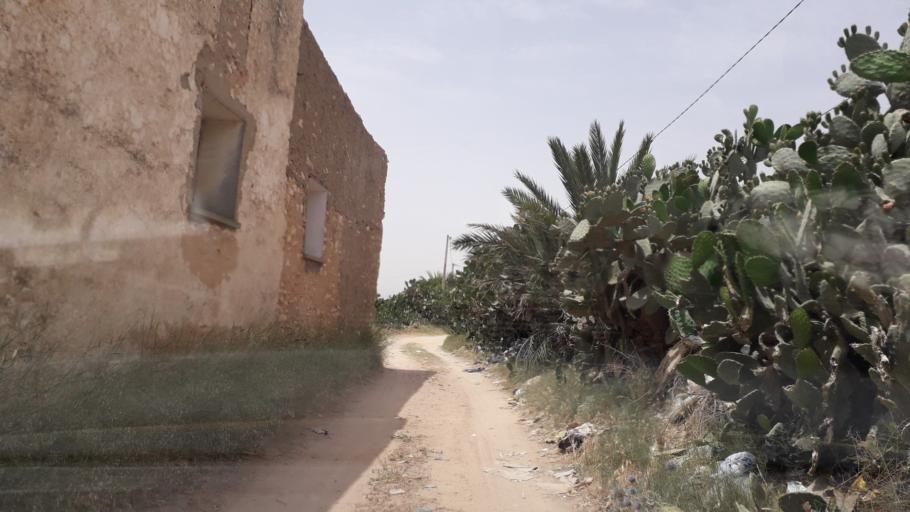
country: TN
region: Safaqis
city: Al Qarmadah
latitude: 34.8538
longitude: 10.7587
